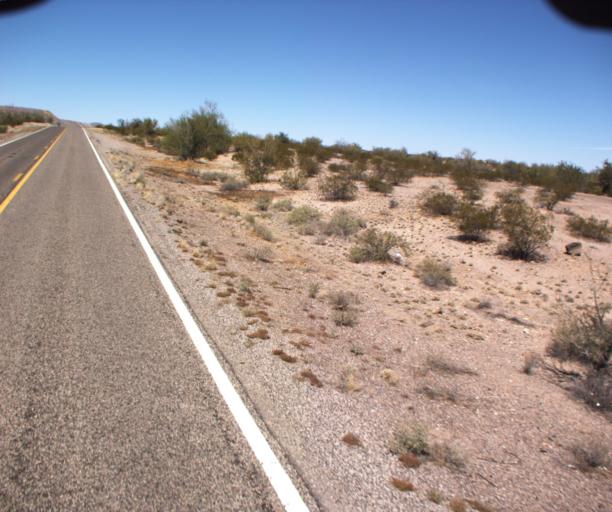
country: US
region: Arizona
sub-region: Pima County
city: Ajo
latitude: 32.3479
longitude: -112.8132
